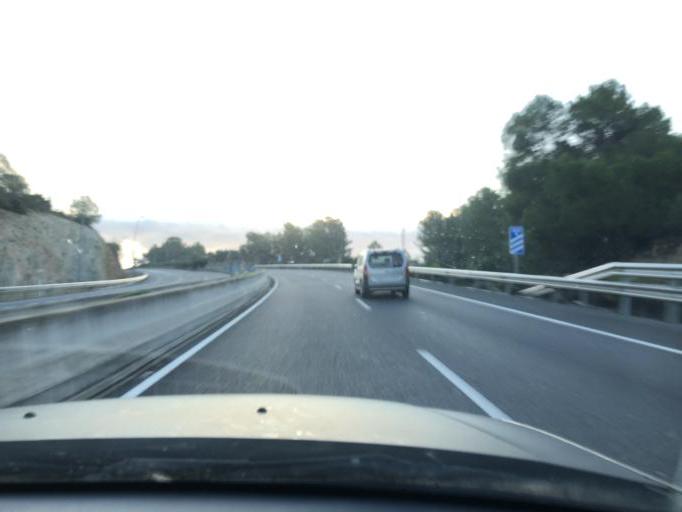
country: ES
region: Balearic Islands
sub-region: Illes Balears
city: Montuiri
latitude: 39.5603
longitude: 3.0042
